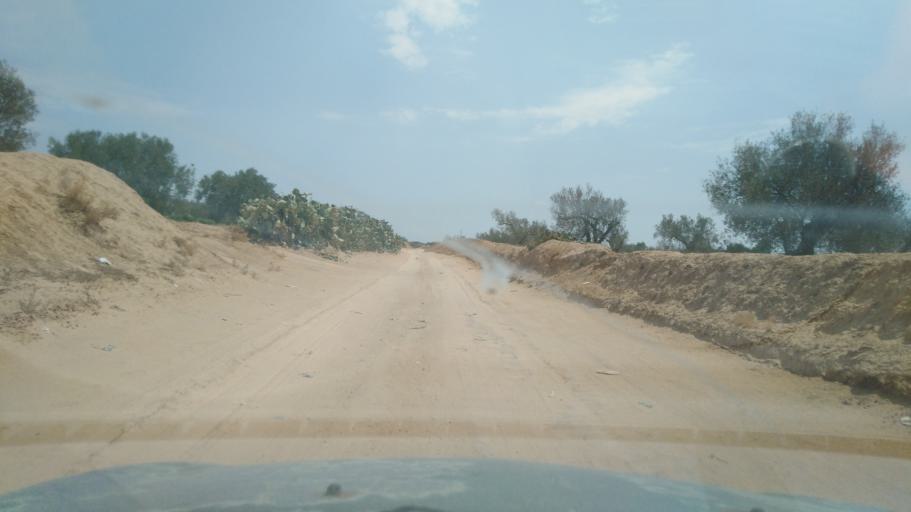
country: TN
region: Safaqis
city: Sfax
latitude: 34.7386
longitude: 10.5522
